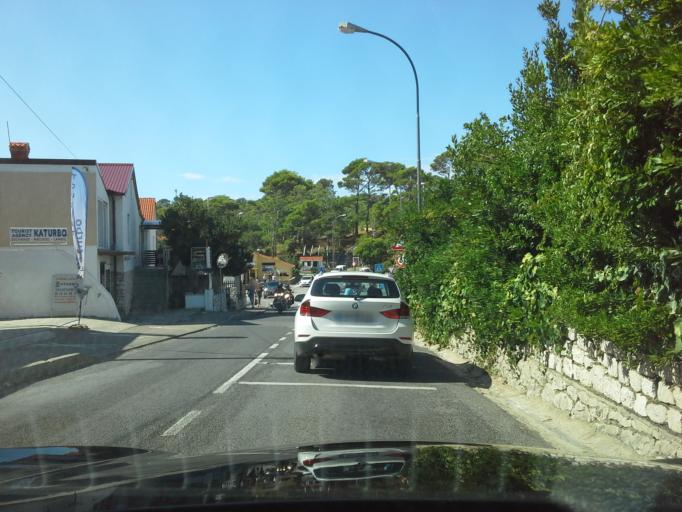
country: HR
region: Primorsko-Goranska
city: Banjol
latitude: 44.7611
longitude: 14.7615
